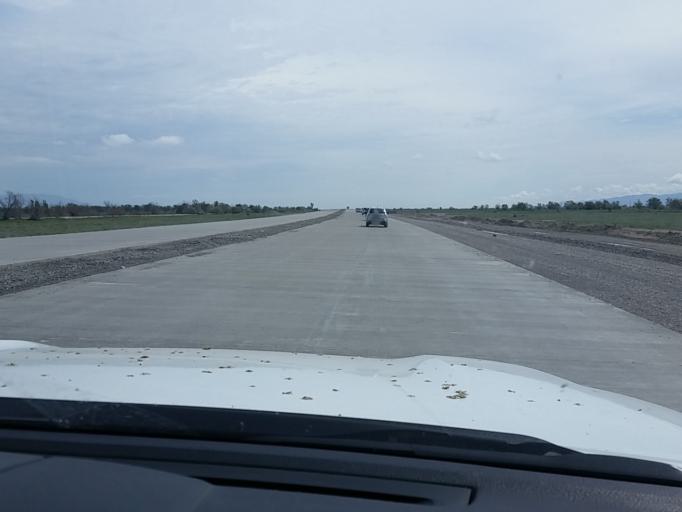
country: KZ
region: Almaty Oblysy
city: Turgen'
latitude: 43.6116
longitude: 78.3407
